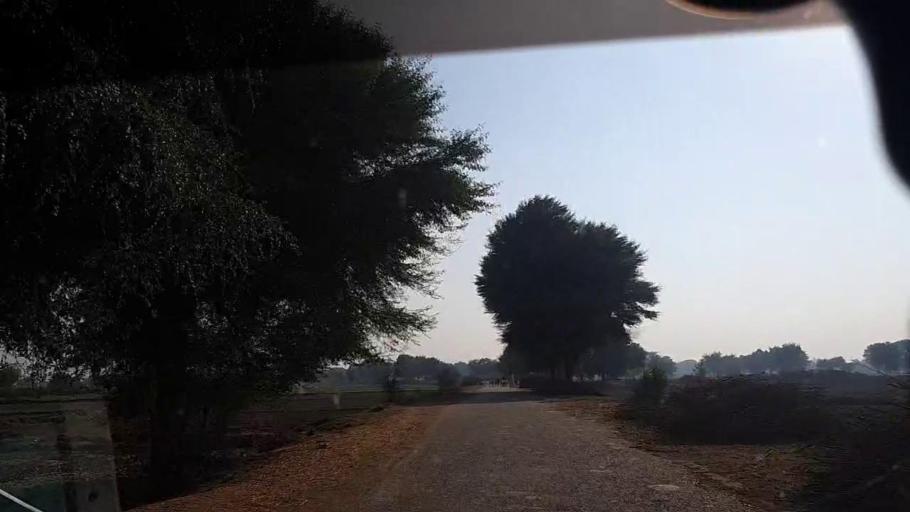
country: PK
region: Sindh
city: Hingorja
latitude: 27.2300
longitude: 68.2692
